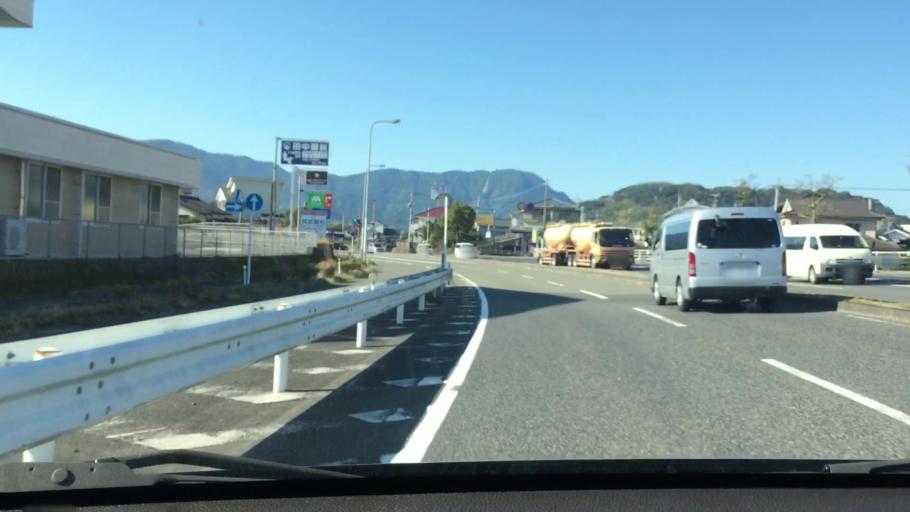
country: JP
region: Kagoshima
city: Kajiki
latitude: 31.7321
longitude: 130.6304
